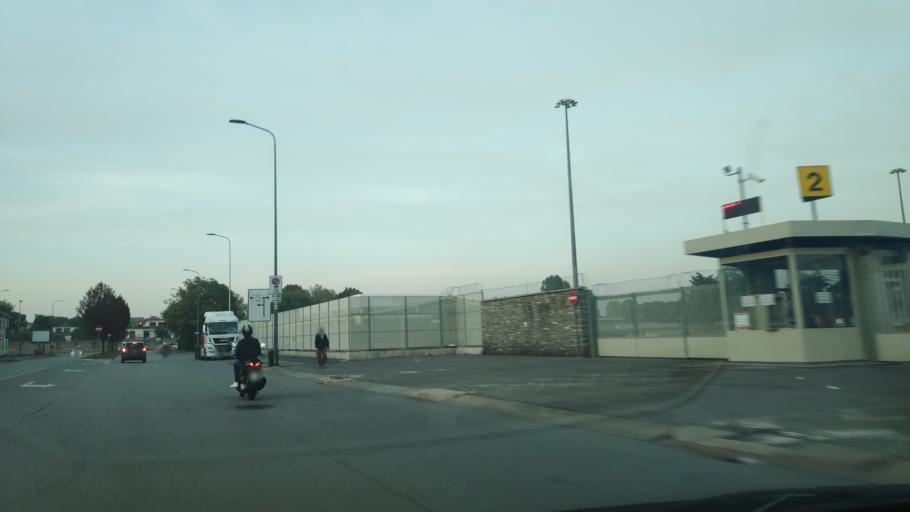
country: IT
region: Lombardy
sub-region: Citta metropolitana di Milano
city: Chiaravalle
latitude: 45.4545
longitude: 9.2294
